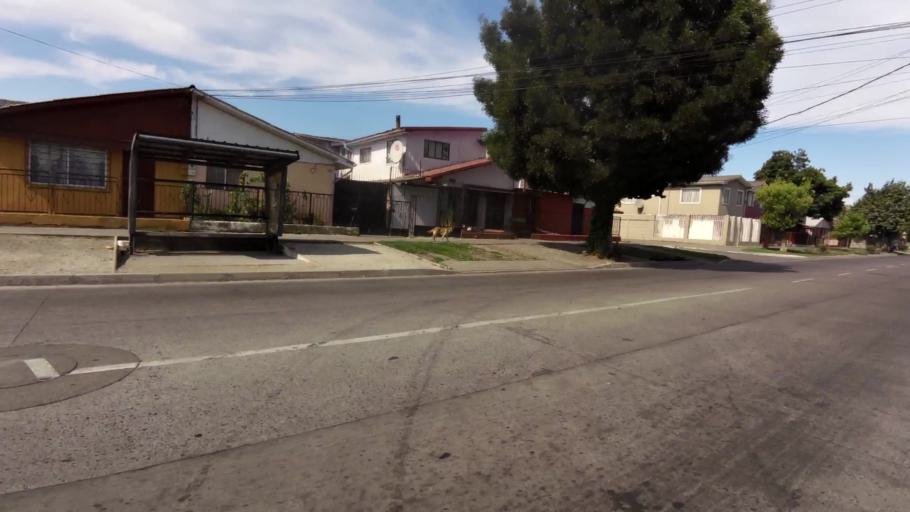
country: CL
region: Biobio
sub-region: Provincia de Concepcion
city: Talcahuano
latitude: -36.7802
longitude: -73.1065
